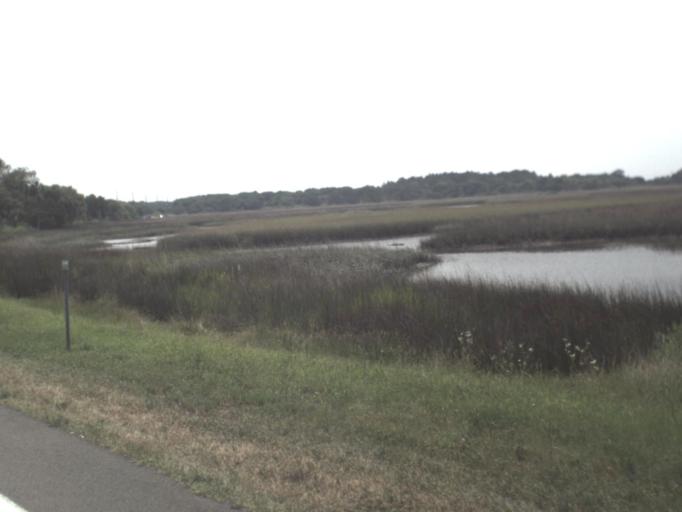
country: US
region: Florida
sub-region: Duval County
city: Atlantic Beach
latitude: 30.4114
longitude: -81.4222
